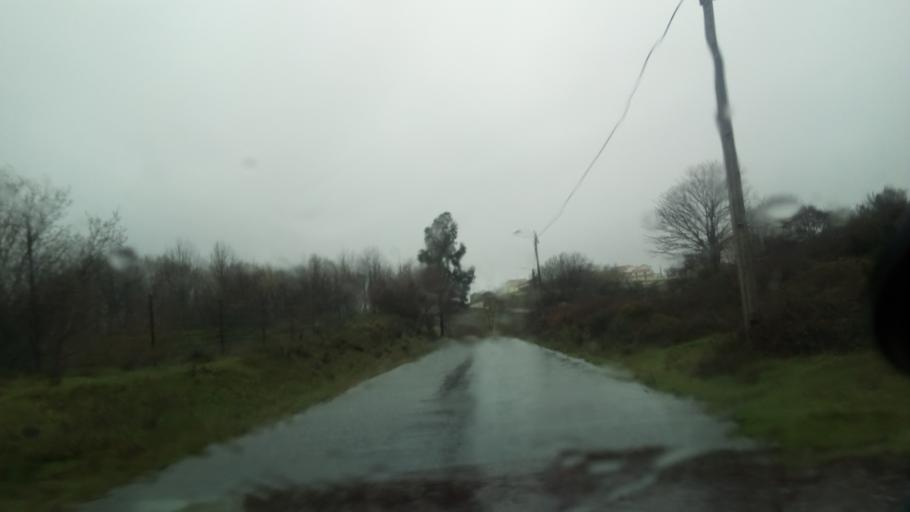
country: PT
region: Guarda
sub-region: Celorico da Beira
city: Celorico da Beira
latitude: 40.5405
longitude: -7.4536
